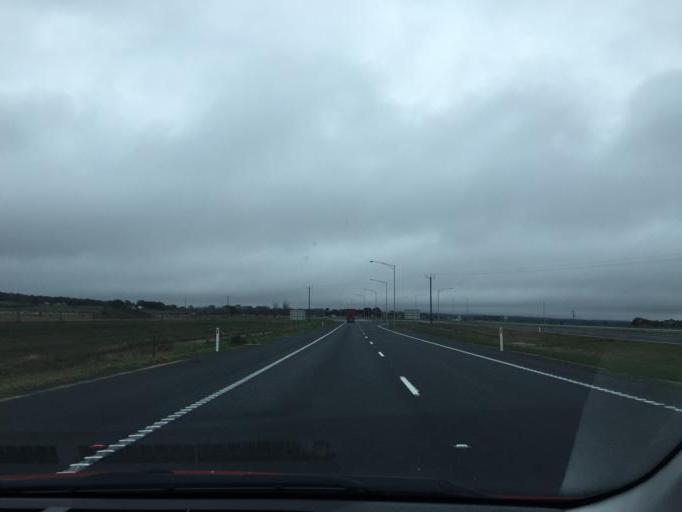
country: AU
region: Victoria
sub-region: Ballarat North
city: Newington
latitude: -37.4380
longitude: 143.4649
